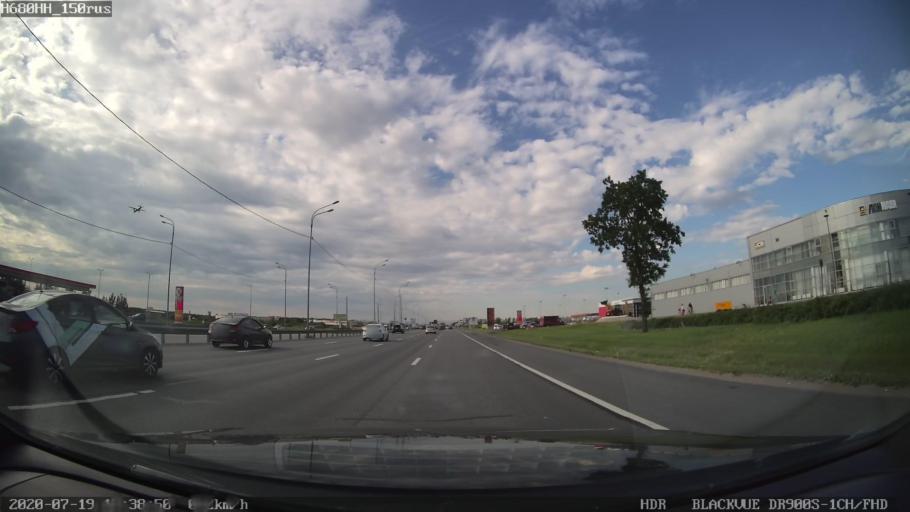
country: RU
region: St.-Petersburg
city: Aleksandrovskaya
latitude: 59.7816
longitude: 30.3257
